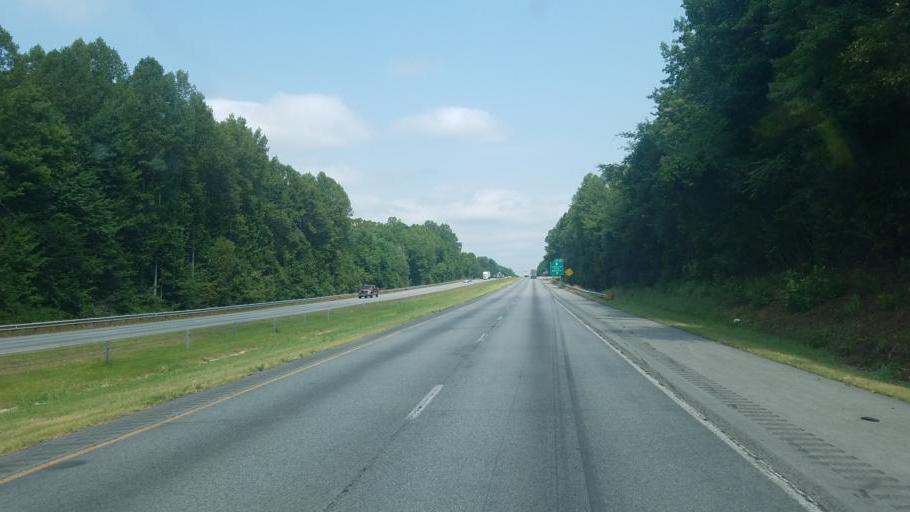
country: US
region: North Carolina
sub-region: Yadkin County
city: Jonesville
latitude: 36.2332
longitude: -80.8157
